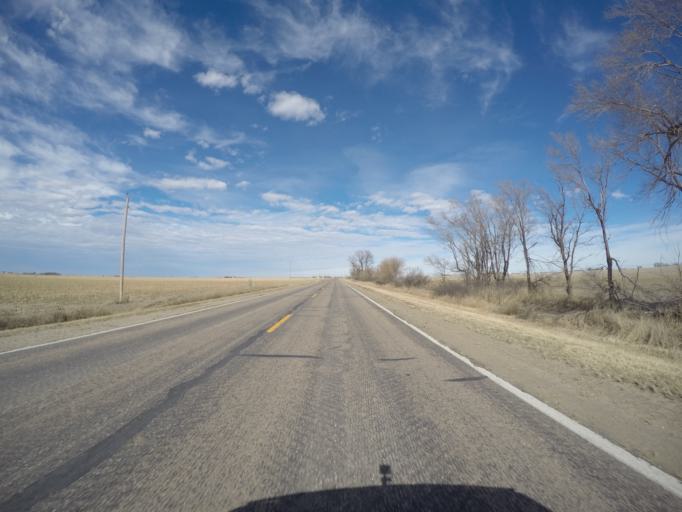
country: US
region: Nebraska
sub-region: Franklin County
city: Franklin
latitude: 40.2567
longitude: -98.9523
